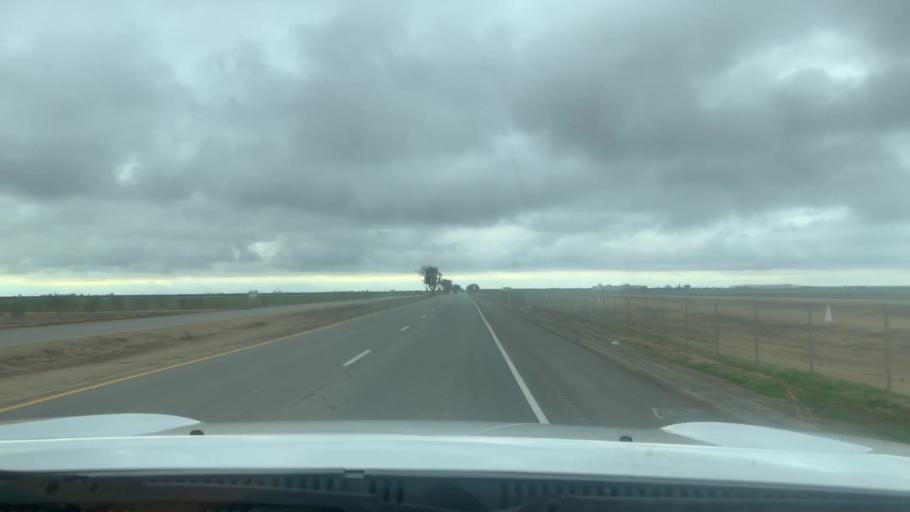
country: US
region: California
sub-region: Kern County
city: Shafter
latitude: 35.4998
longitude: -119.1867
